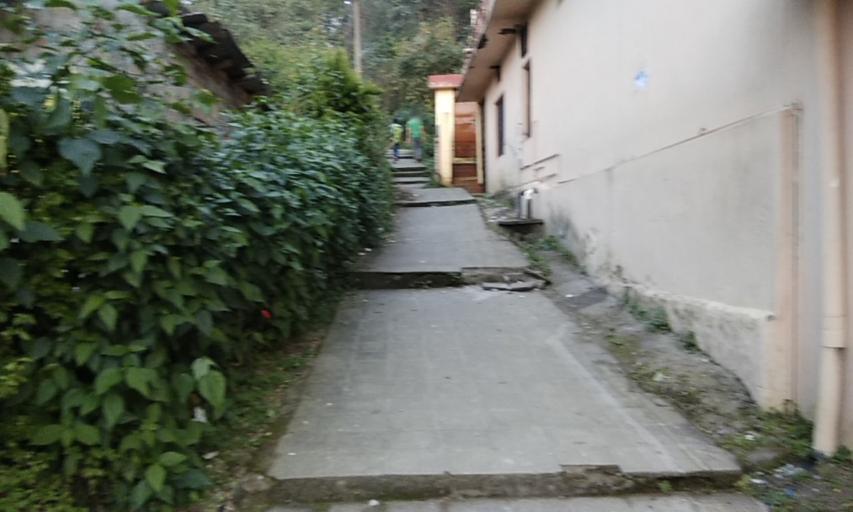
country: IN
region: Himachal Pradesh
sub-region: Kangra
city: Palampur
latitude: 32.1146
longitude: 76.5352
